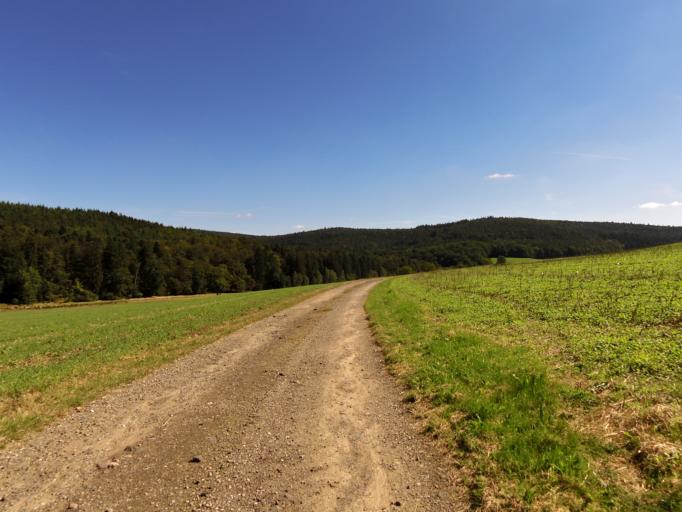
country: DE
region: Hesse
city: Reichelsheim
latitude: 49.6491
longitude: 8.8738
